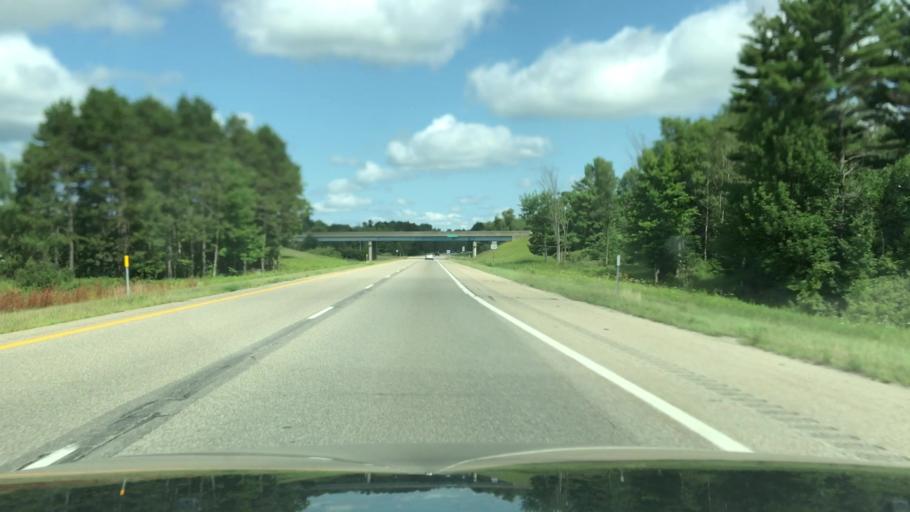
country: US
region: Michigan
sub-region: Mecosta County
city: Big Rapids
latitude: 43.6936
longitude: -85.5238
